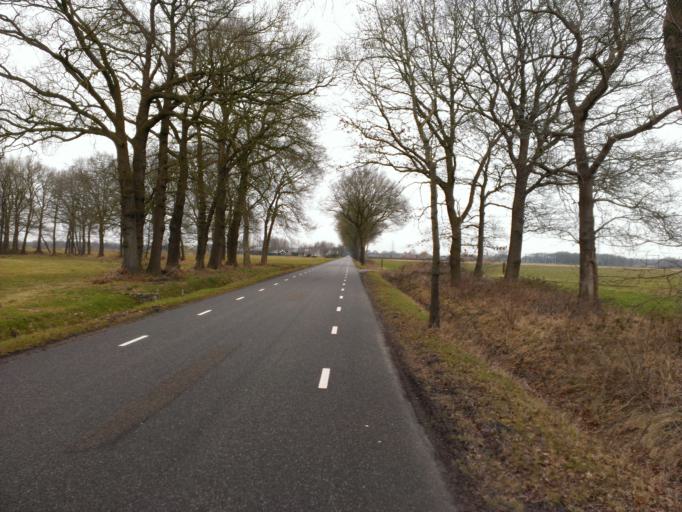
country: NL
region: Drenthe
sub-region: Gemeente Hoogeveen
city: Hoogeveen
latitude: 52.7450
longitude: 6.4771
